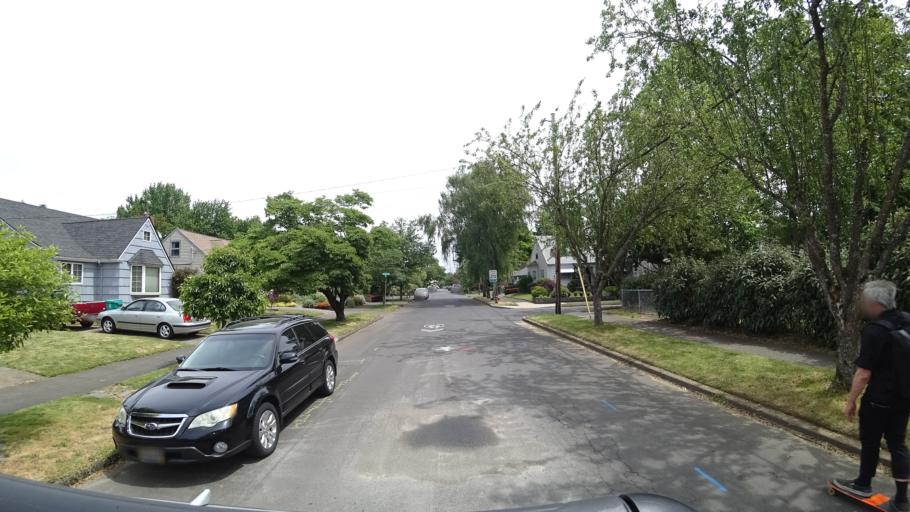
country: US
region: Oregon
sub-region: Multnomah County
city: Portland
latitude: 45.5251
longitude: -122.6124
